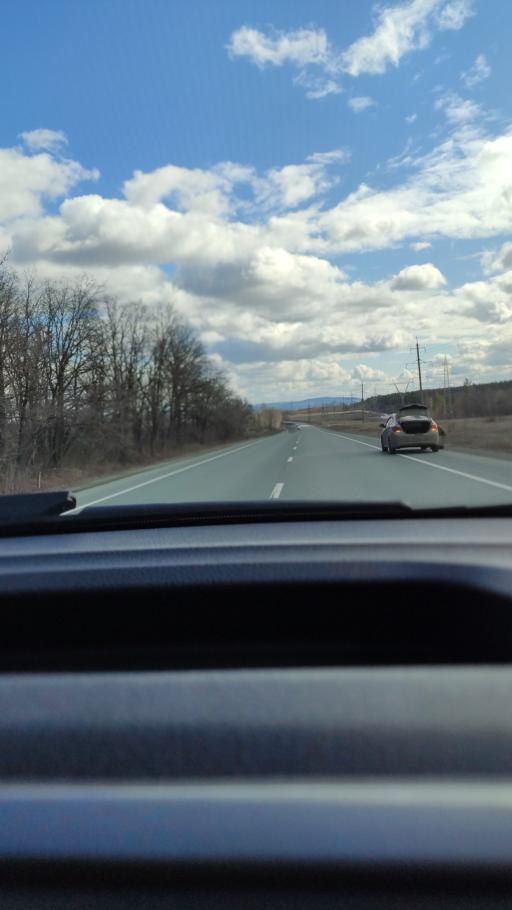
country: RU
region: Samara
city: Bogatyr'
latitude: 53.4973
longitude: 49.9598
